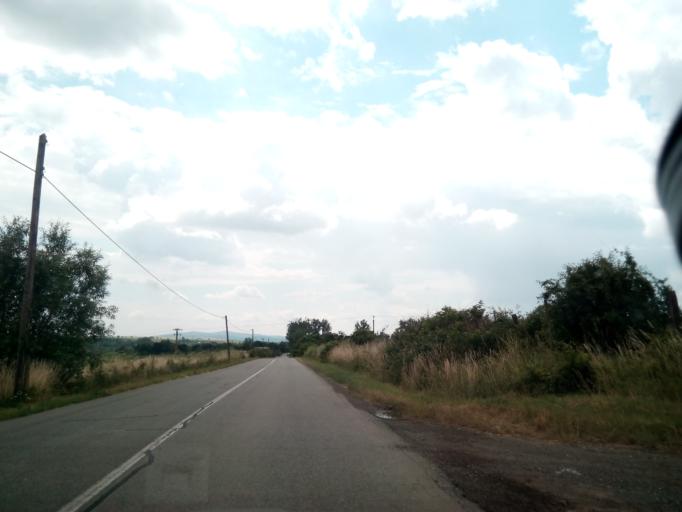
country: SK
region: Kosicky
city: Secovce
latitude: 48.5927
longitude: 21.5618
